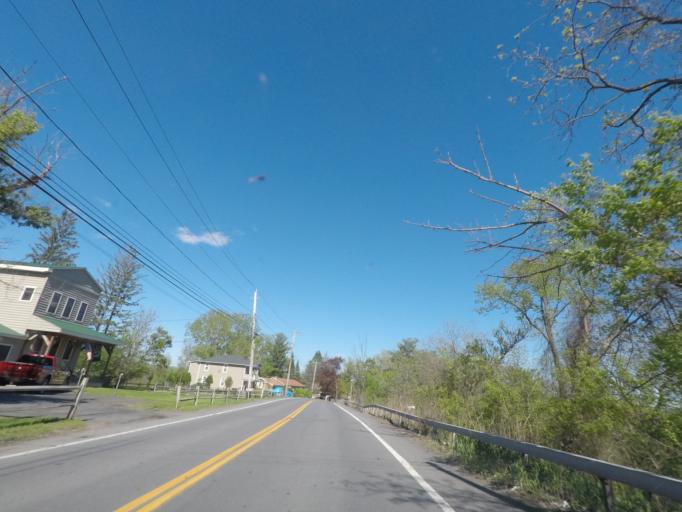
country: US
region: New York
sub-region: Albany County
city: Albany
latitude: 42.6204
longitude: -73.7762
